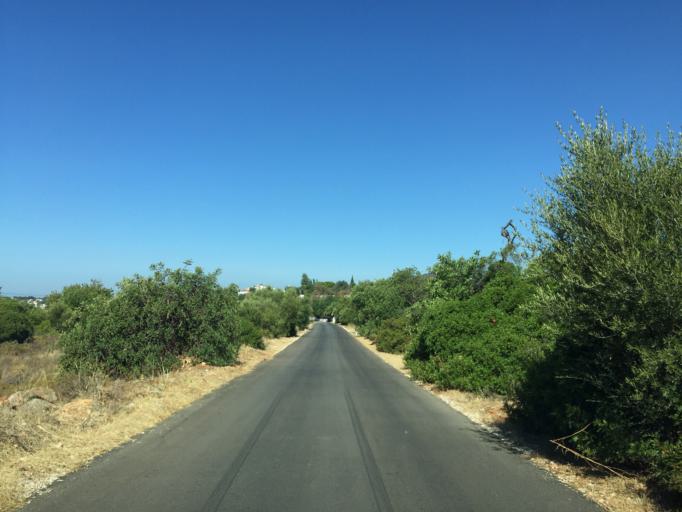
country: PT
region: Faro
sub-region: Loule
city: Almancil
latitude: 37.0991
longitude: -8.0359
